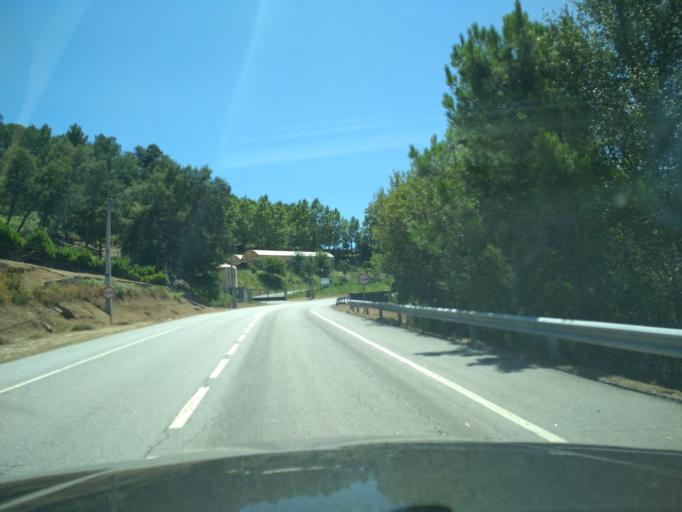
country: PT
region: Vila Real
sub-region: Ribeira de Pena
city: Sobreira
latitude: 41.5283
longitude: -7.7845
